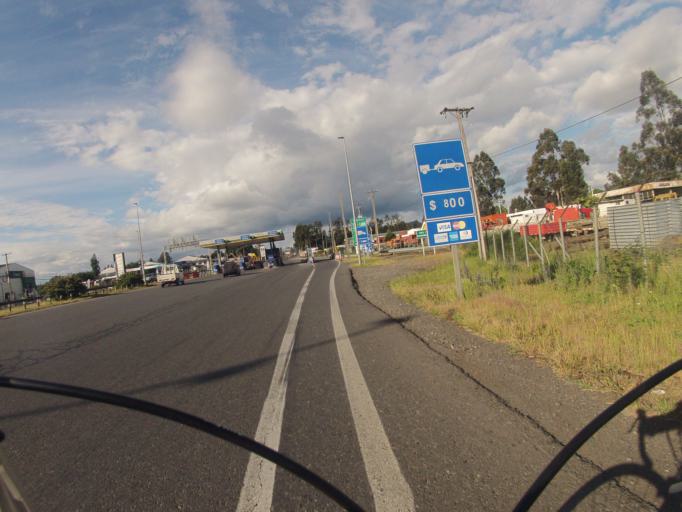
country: CL
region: Araucania
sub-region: Provincia de Cautin
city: Temuco
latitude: -38.7828
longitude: -72.6119
